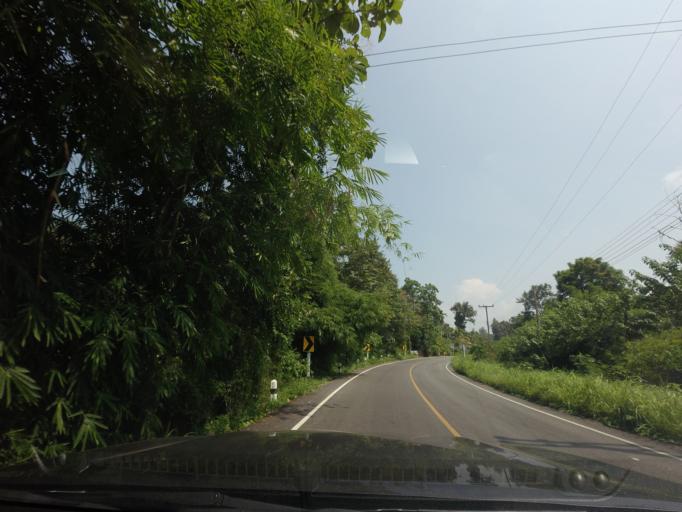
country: TH
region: Nan
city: Nan
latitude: 18.8341
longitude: 100.7768
